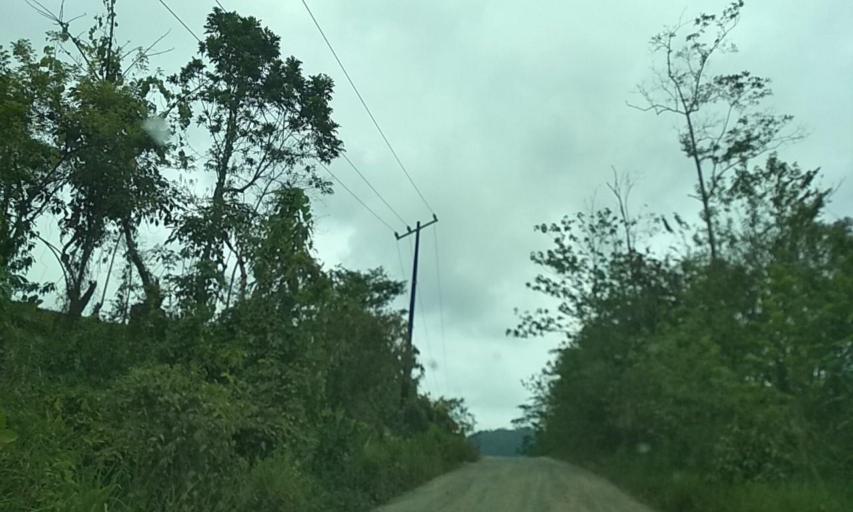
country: MX
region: Veracruz
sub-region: Uxpanapa
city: Poblado 10
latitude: 17.4859
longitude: -94.1275
